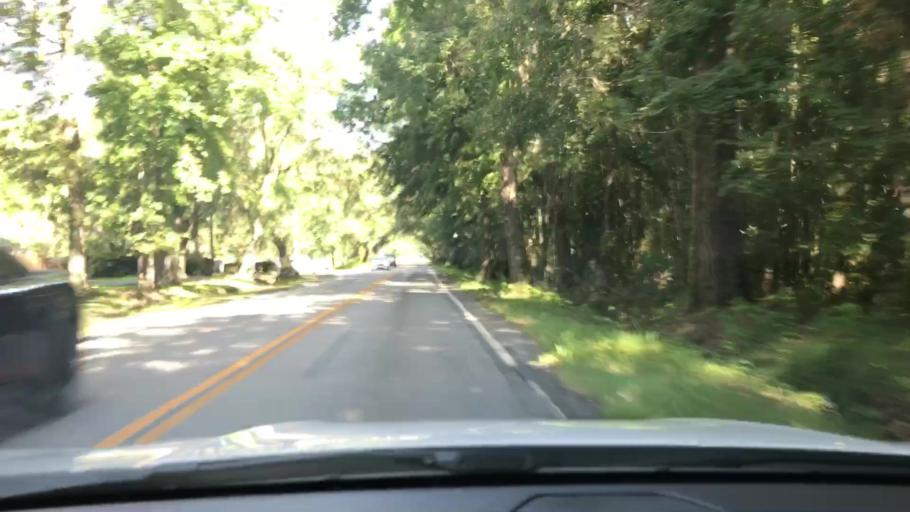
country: US
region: South Carolina
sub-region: Charleston County
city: Shell Point
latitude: 32.8487
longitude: -80.0641
